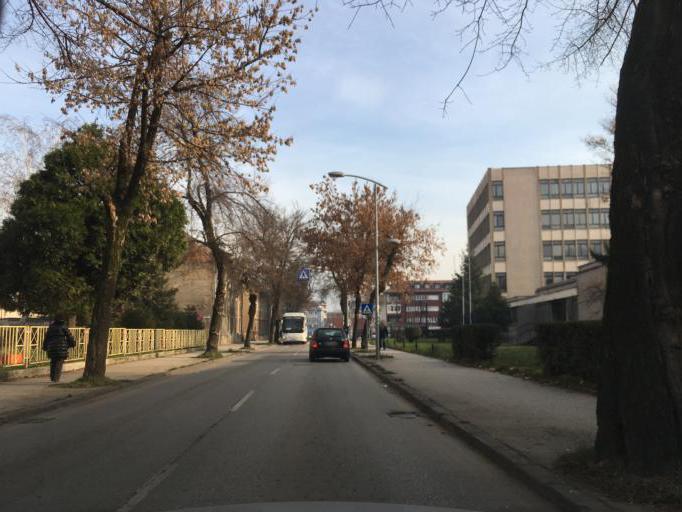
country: BA
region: Federation of Bosnia and Herzegovina
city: Zenica
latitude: 44.2004
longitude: 17.9008
